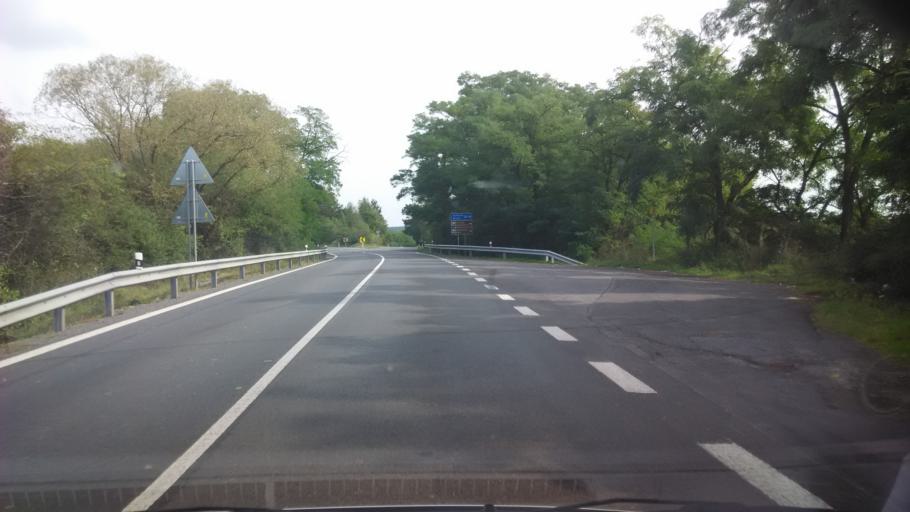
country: SK
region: Banskobystricky
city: Krupina
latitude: 48.3132
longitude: 19.0362
